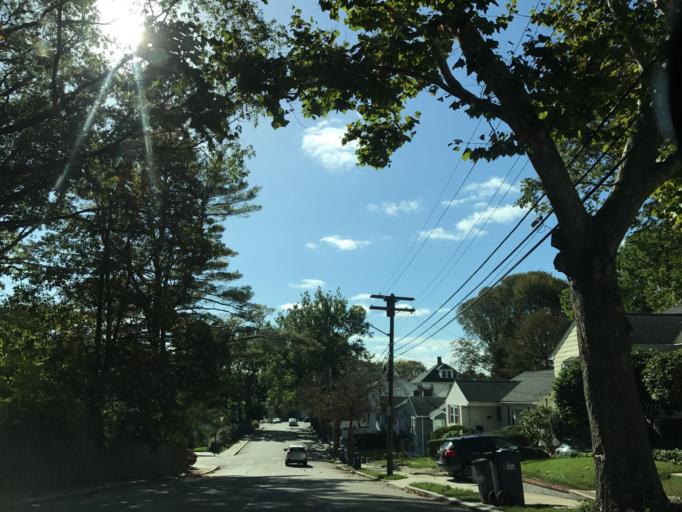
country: US
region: Massachusetts
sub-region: Norfolk County
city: Milton
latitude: 42.2752
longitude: -71.0782
